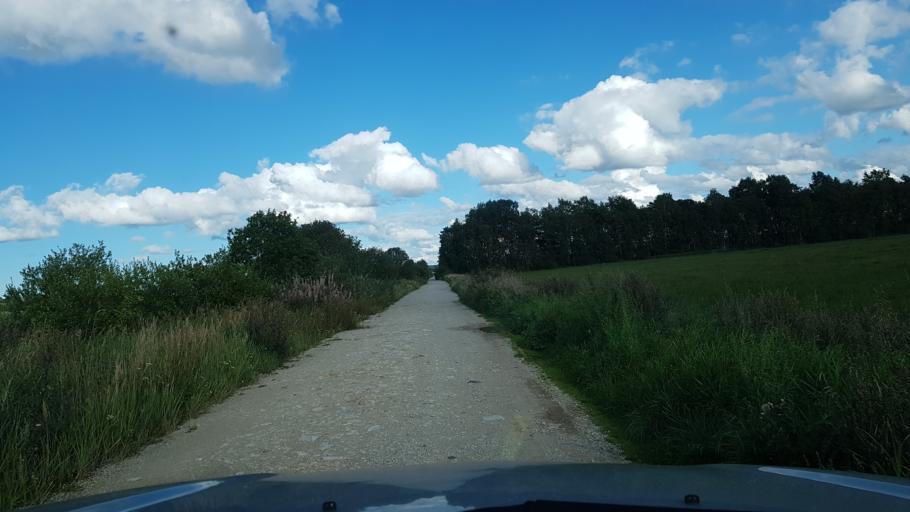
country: EE
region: Harju
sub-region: Kiili vald
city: Kiili
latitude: 59.3562
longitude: 24.8440
